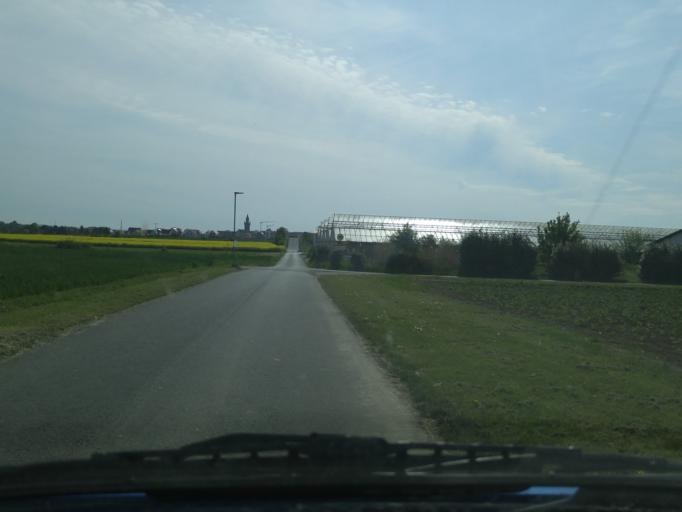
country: DE
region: Hesse
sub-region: Regierungsbezirk Darmstadt
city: Bad Nauheim
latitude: 50.3435
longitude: 8.7306
